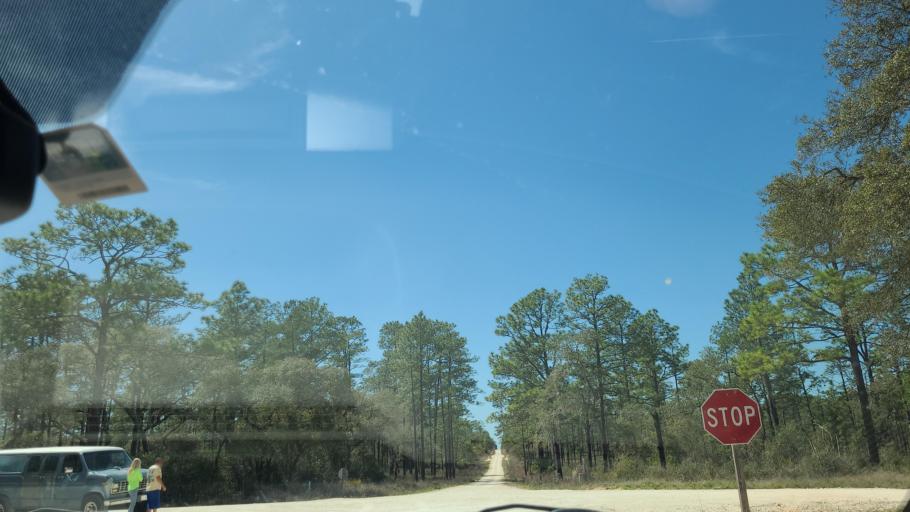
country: US
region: Florida
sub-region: Putnam County
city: Interlachen
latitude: 29.4288
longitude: -81.8084
